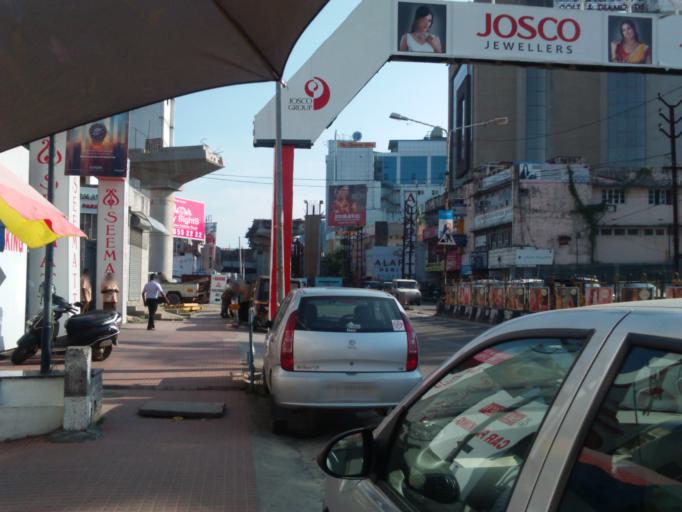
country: IN
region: Kerala
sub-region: Ernakulam
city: Cochin
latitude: 9.9853
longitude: 76.2818
